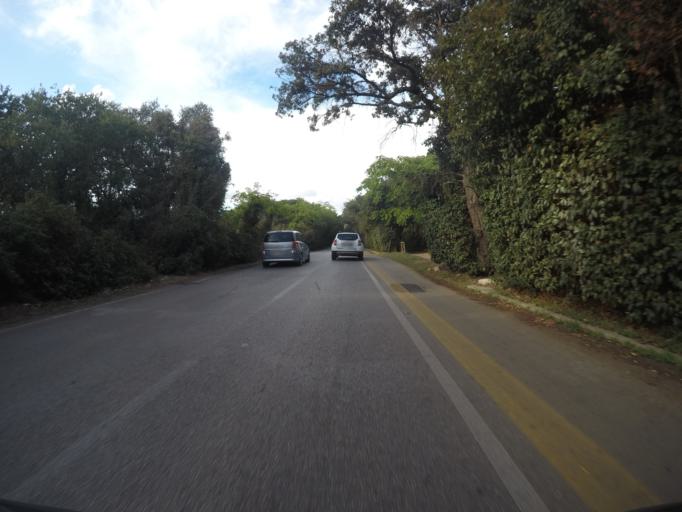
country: IT
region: Sicily
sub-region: Palermo
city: Palermo
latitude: 38.1680
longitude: 13.3391
